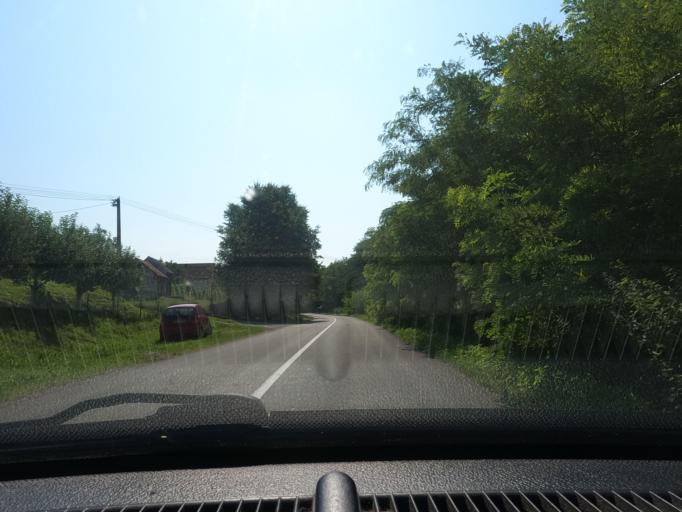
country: RS
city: Kozjak
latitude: 44.5457
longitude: 19.2990
